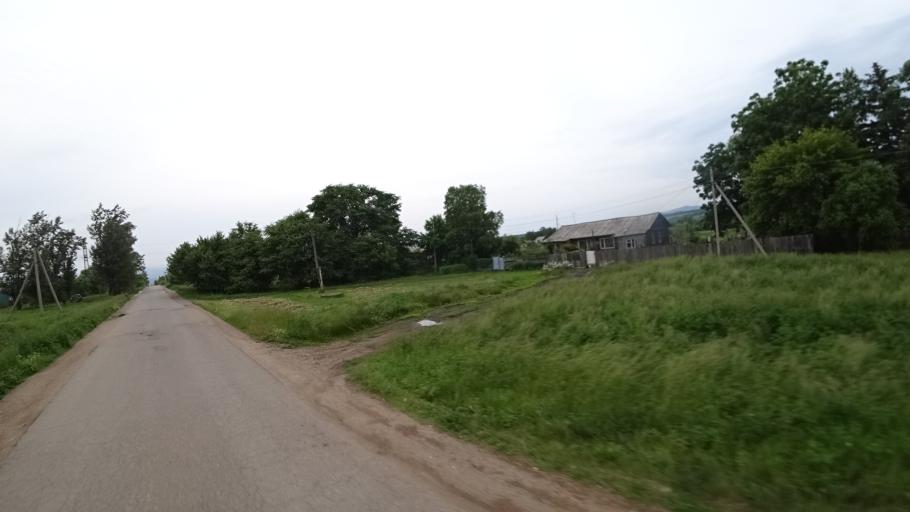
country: RU
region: Primorskiy
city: Novosysoyevka
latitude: 44.2305
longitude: 133.3607
